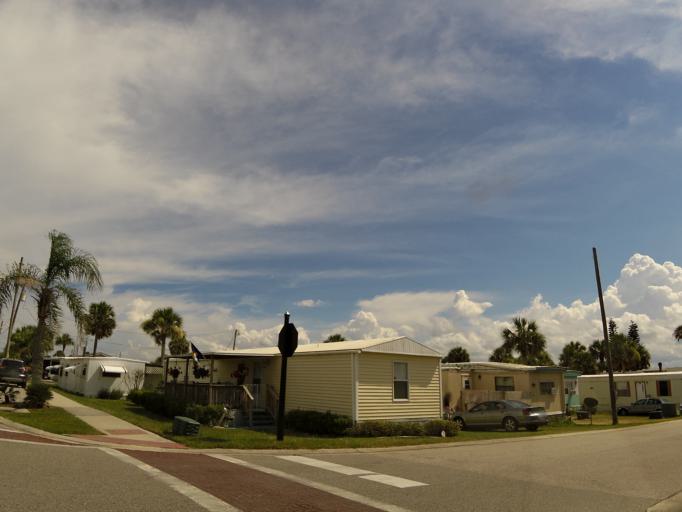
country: US
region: Florida
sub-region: Flagler County
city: Flagler Beach
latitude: 29.4778
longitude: -81.1282
